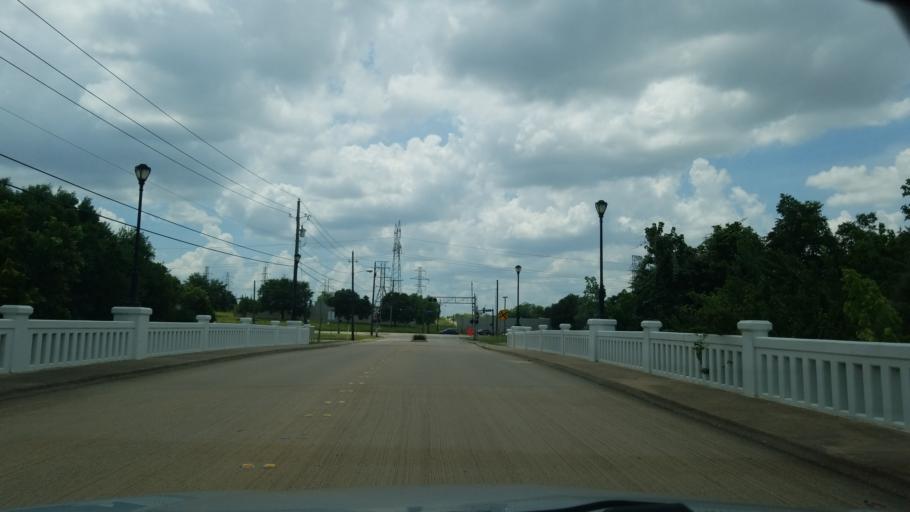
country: US
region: Texas
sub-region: Dallas County
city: Coppell
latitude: 32.9563
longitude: -96.9767
